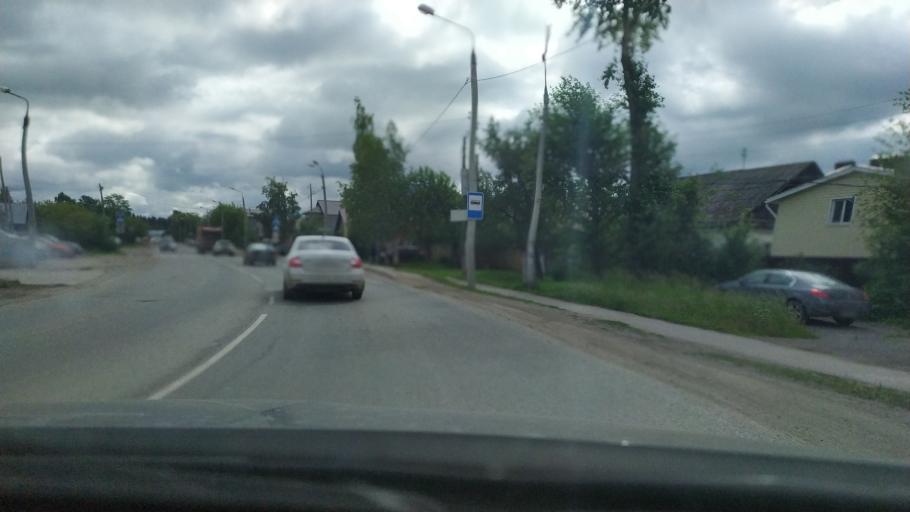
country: RU
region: Perm
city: Froly
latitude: 57.9771
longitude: 56.3060
